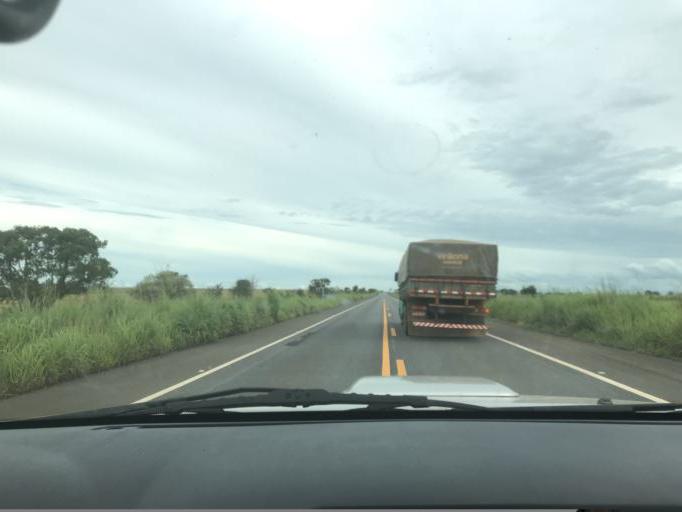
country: BR
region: Minas Gerais
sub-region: Araxa
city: Araxa
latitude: -19.3859
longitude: -46.8598
